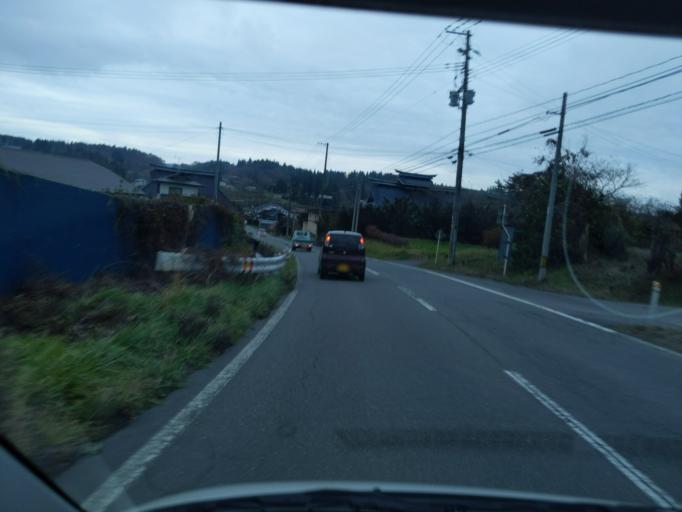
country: JP
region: Iwate
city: Ichinoseki
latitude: 39.0231
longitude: 141.3312
